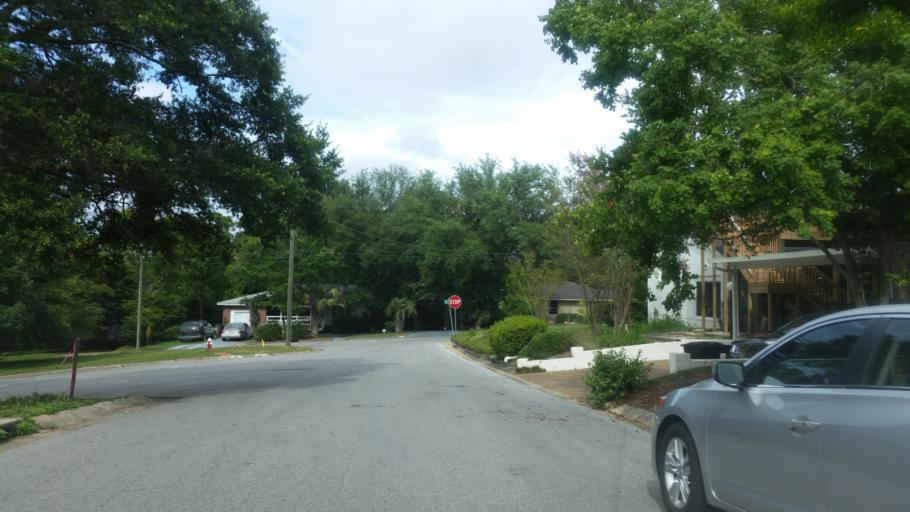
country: US
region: Florida
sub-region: Escambia County
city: East Pensacola Heights
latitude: 30.4444
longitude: -87.1912
